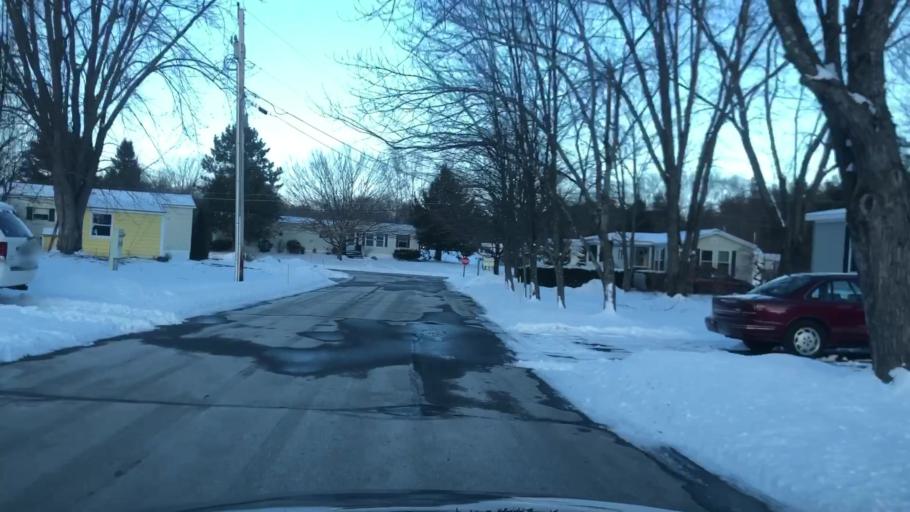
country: US
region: New Hampshire
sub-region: Hillsborough County
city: Milford
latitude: 42.8162
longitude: -71.6653
